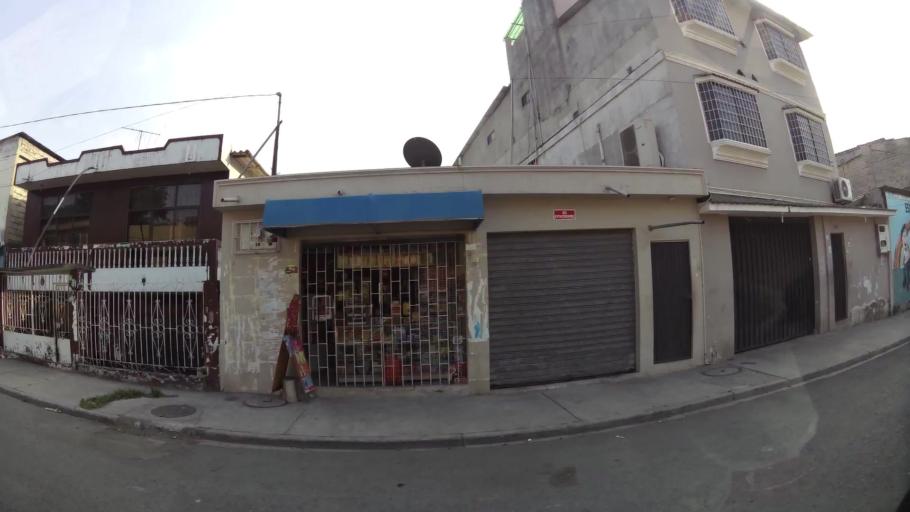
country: EC
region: Guayas
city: Guayaquil
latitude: -2.1546
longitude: -79.9115
